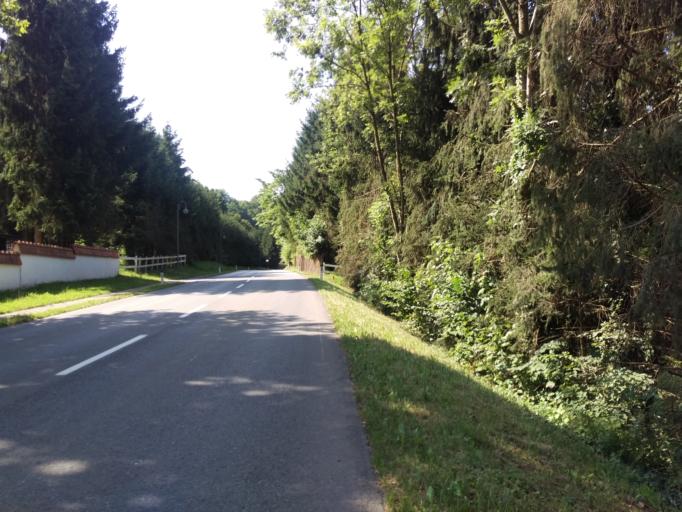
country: AT
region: Styria
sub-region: Politischer Bezirk Graz-Umgebung
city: Mellach
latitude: 46.9367
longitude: 15.5112
